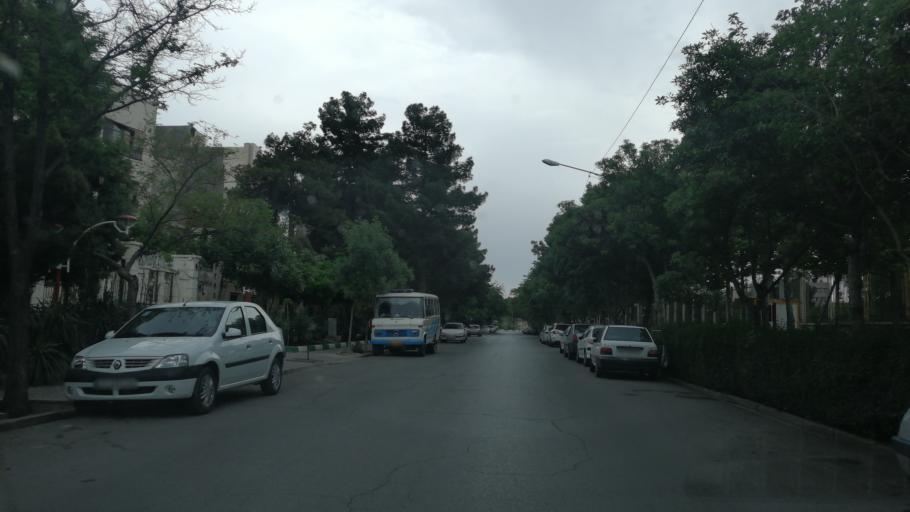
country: IR
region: Razavi Khorasan
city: Mashhad
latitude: 36.2881
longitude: 59.5814
